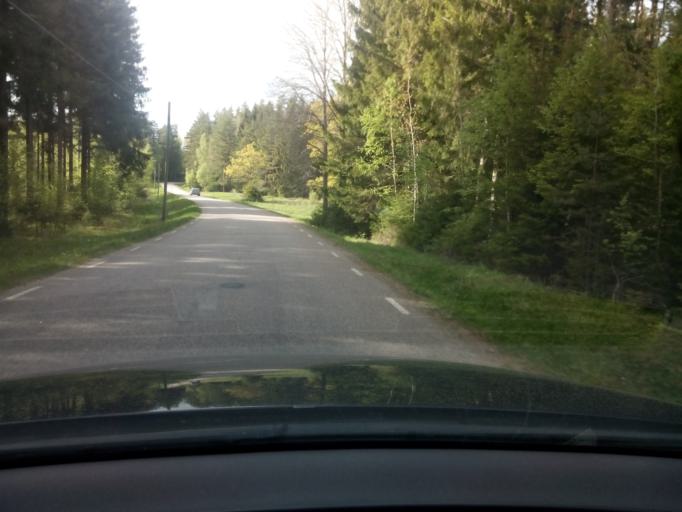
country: SE
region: Soedermanland
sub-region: Nykopings Kommun
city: Stigtomta
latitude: 58.9107
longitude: 16.8825
